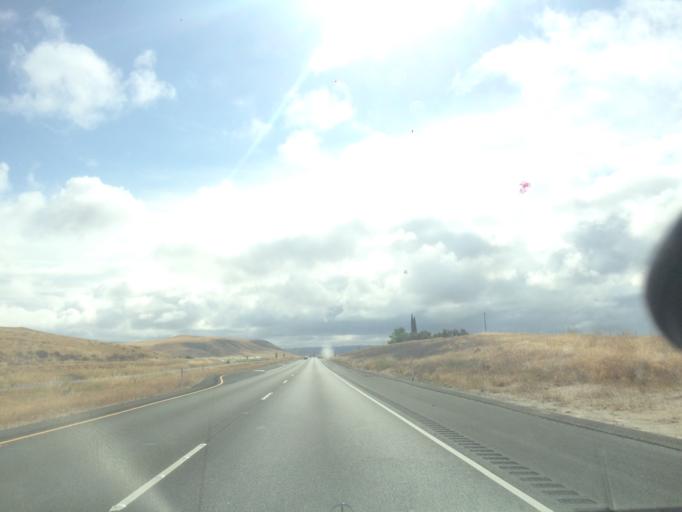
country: US
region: California
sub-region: San Luis Obispo County
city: Shandon
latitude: 35.6595
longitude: -120.4684
